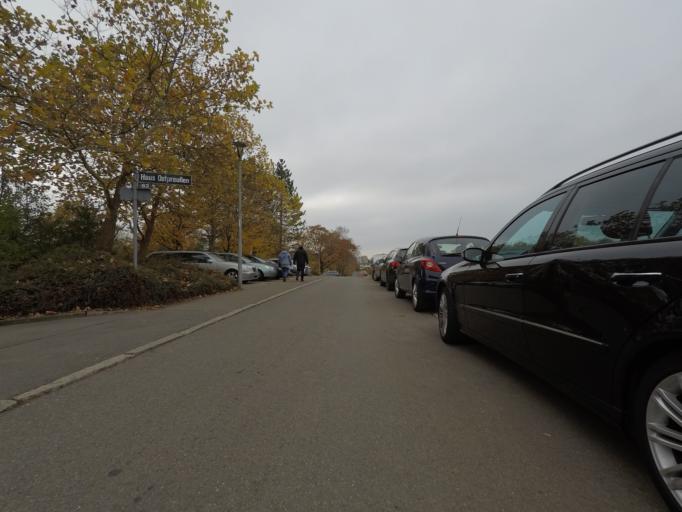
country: DE
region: Baden-Wuerttemberg
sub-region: Tuebingen Region
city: Reutlingen
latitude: 48.5140
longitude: 9.2093
